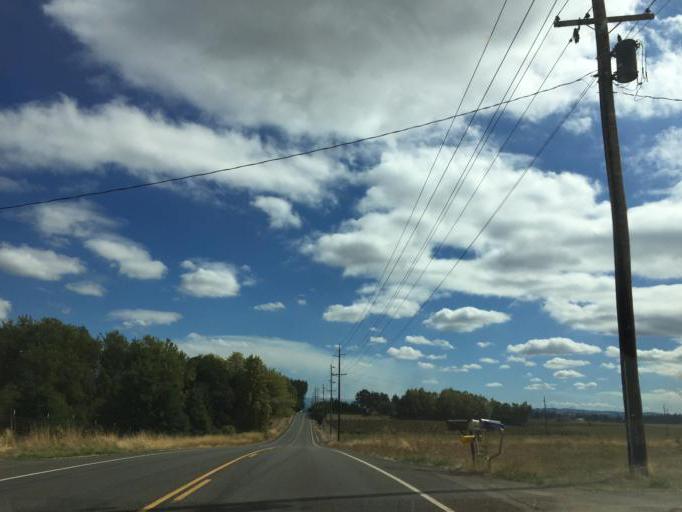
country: US
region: Oregon
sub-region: Marion County
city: Mount Angel
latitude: 45.1157
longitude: -122.7931
